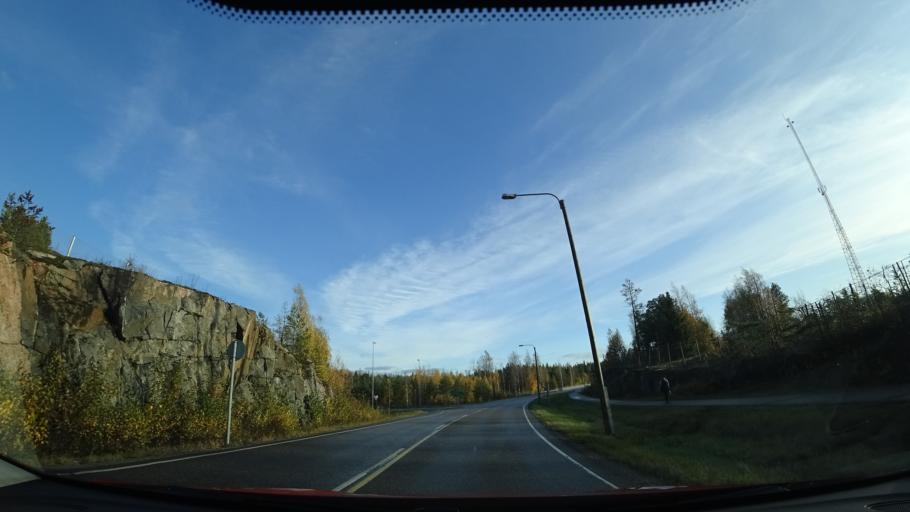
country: FI
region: Uusimaa
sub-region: Helsinki
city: Sibbo
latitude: 60.2682
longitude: 25.2077
